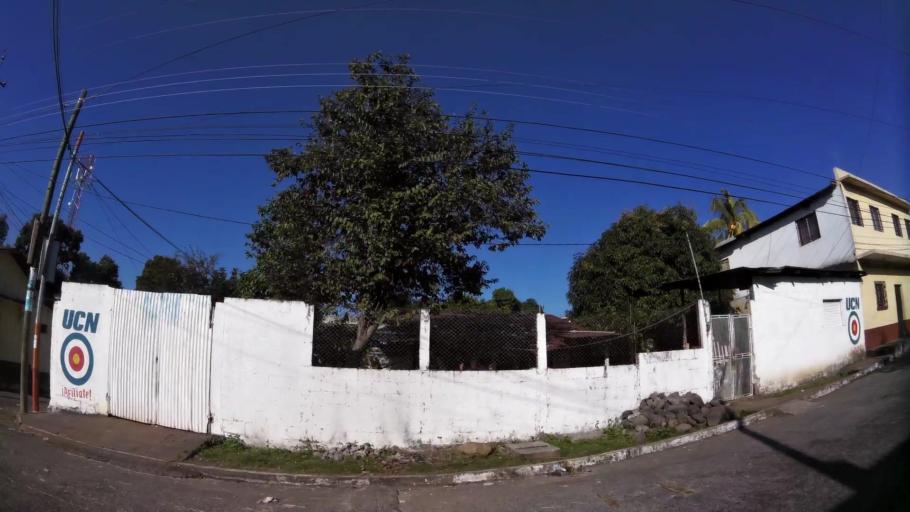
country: GT
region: Suchitepeque
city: Mazatenango
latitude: 14.5295
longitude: -91.5152
